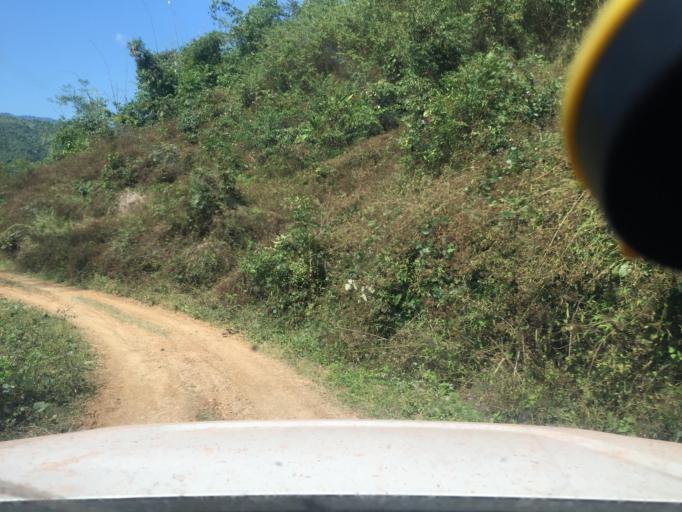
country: LA
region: Phongsali
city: Phongsali
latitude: 21.6489
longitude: 102.4089
